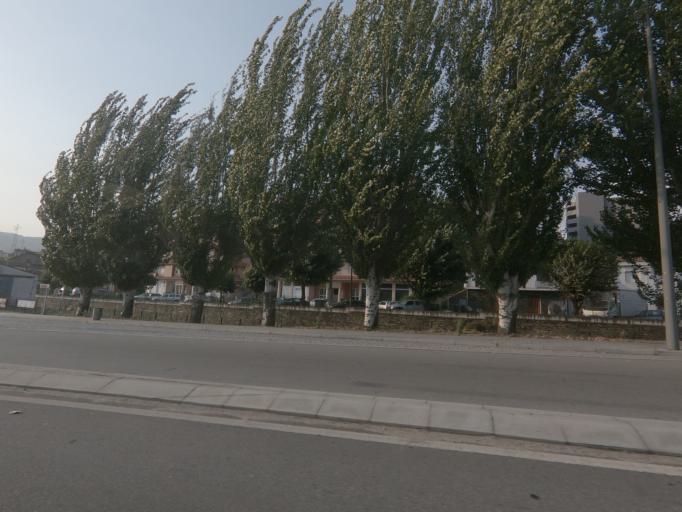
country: PT
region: Vila Real
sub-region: Peso da Regua
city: Peso da Regua
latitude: 41.1560
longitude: -7.7788
